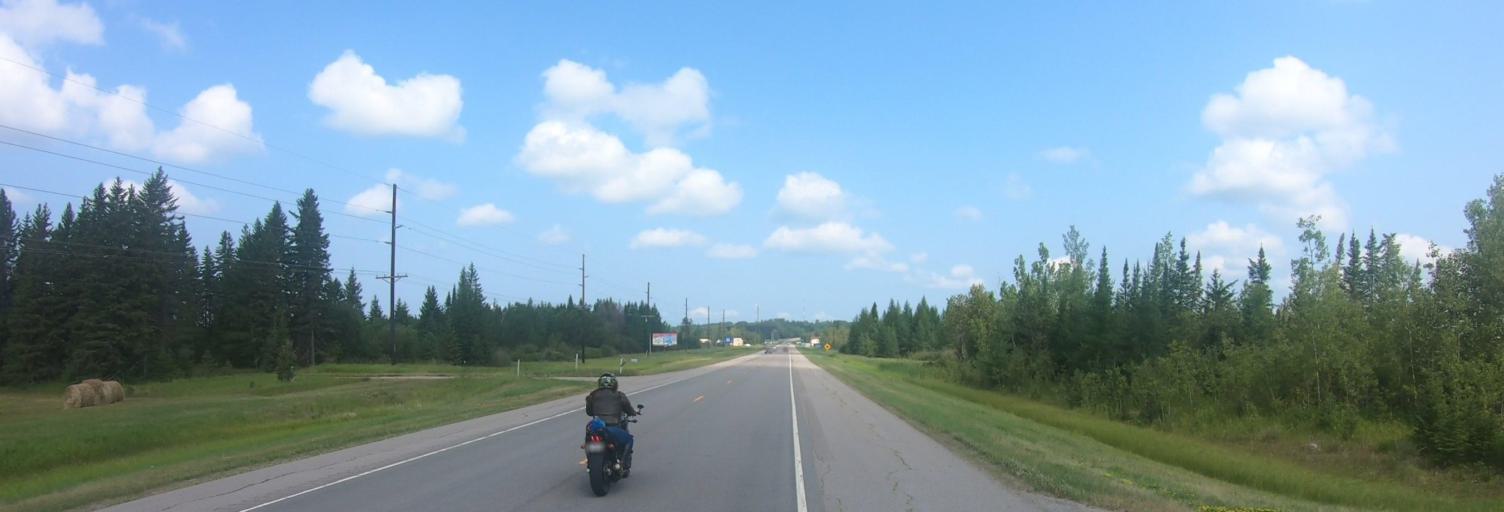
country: US
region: Minnesota
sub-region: Saint Louis County
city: Chisholm
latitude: 47.9584
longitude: -92.8292
